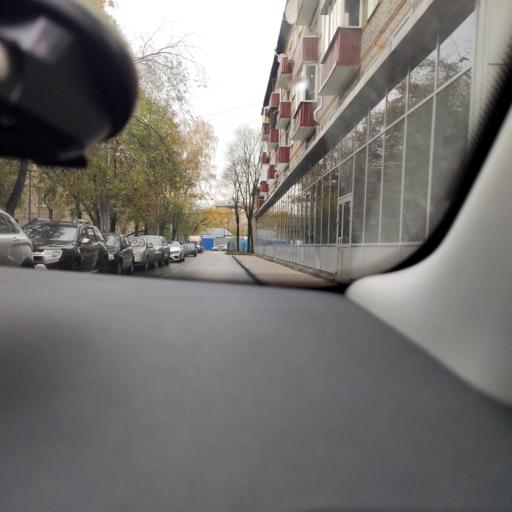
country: RU
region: Moskovskaya
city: Koptevo
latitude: 55.8136
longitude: 37.4920
